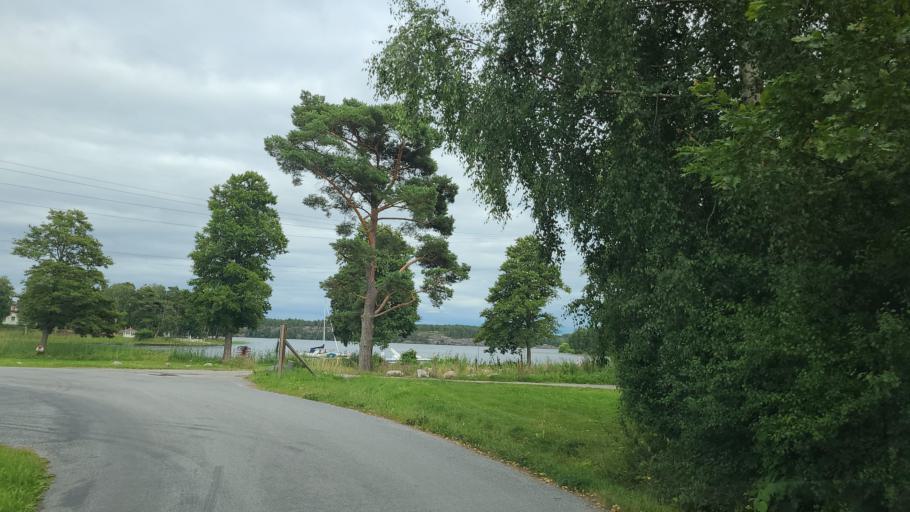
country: SE
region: Stockholm
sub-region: Upplands-Bro Kommun
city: Bro
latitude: 59.4755
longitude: 17.5600
